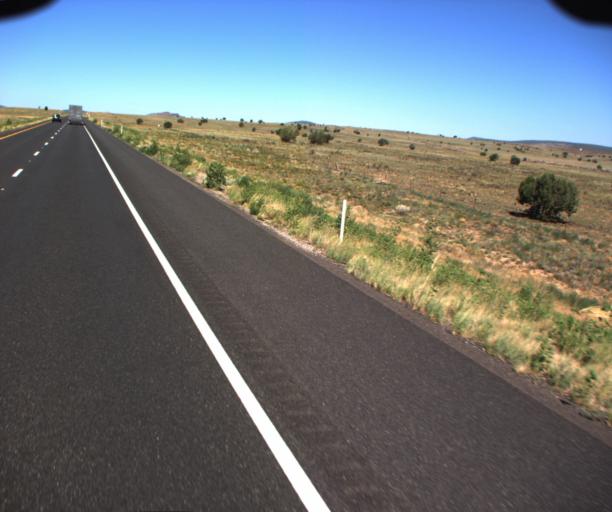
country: US
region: Arizona
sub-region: Yavapai County
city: Paulden
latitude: 35.2332
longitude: -112.6132
